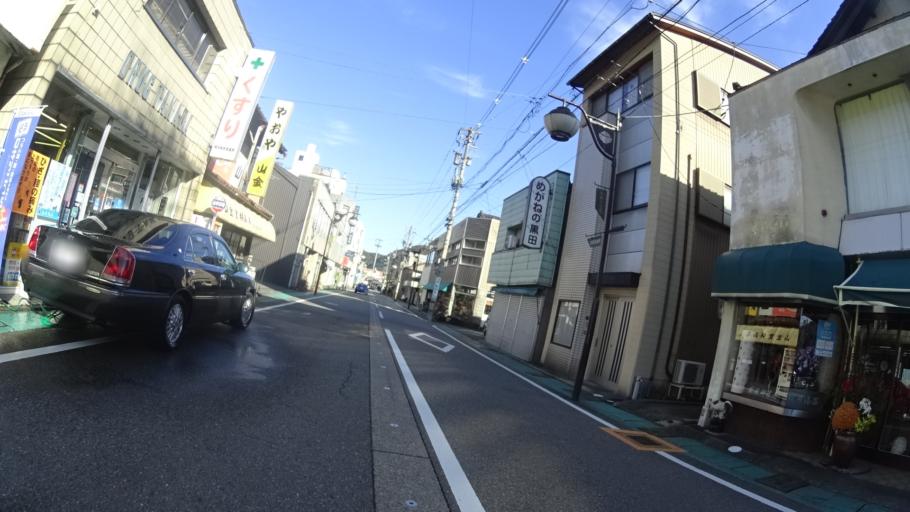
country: JP
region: Fukui
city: Maruoka
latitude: 36.2480
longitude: 136.3745
